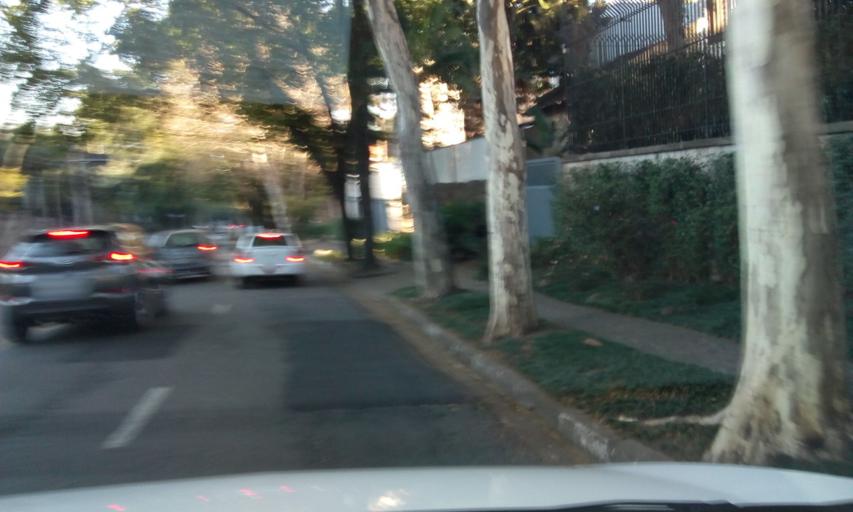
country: BR
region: Sao Paulo
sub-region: Sao Paulo
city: Sao Paulo
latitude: -23.5944
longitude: -46.6974
